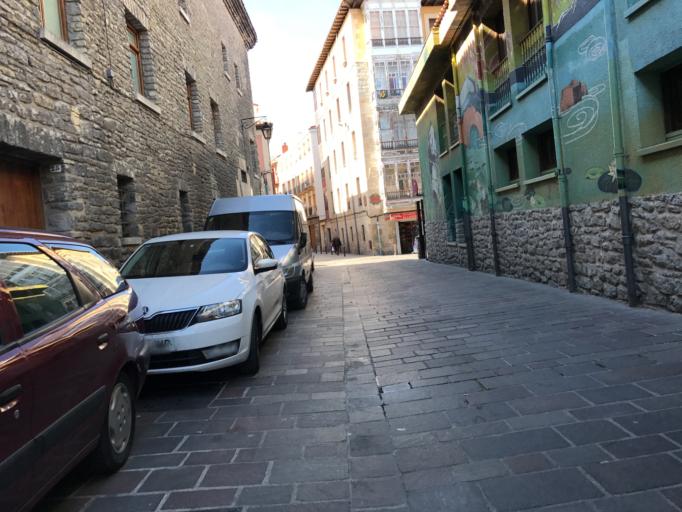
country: ES
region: Basque Country
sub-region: Provincia de Alava
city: Gasteiz / Vitoria
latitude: 42.8513
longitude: -2.6710
